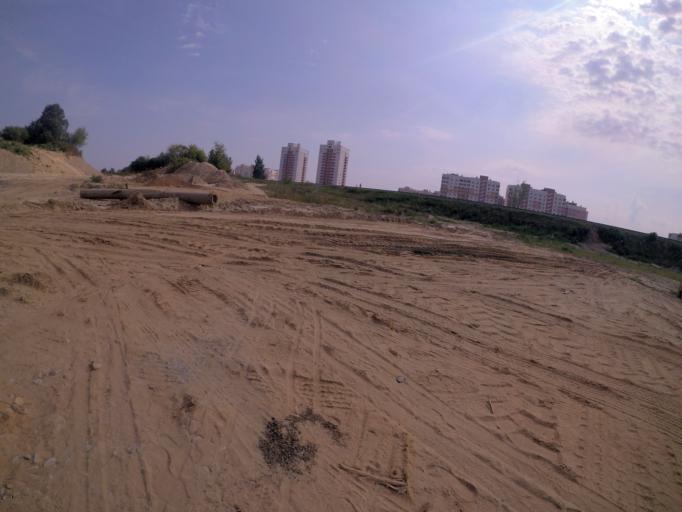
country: BY
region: Grodnenskaya
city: Hrodna
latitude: 53.7162
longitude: 23.8609
